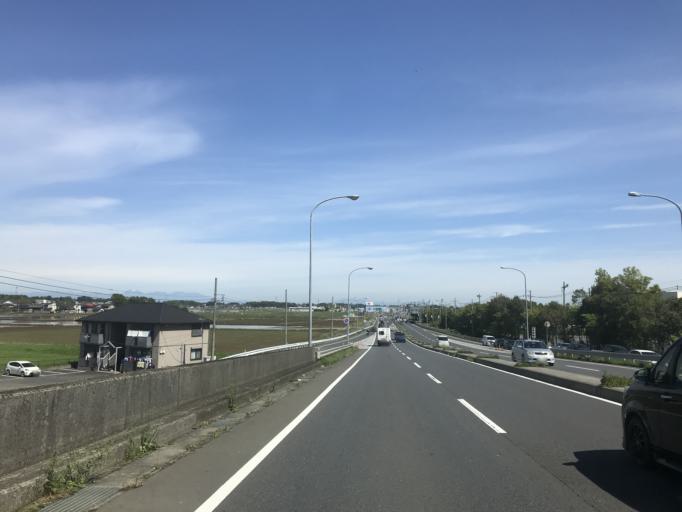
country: JP
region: Ibaraki
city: Ishige
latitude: 36.1886
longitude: 139.9883
